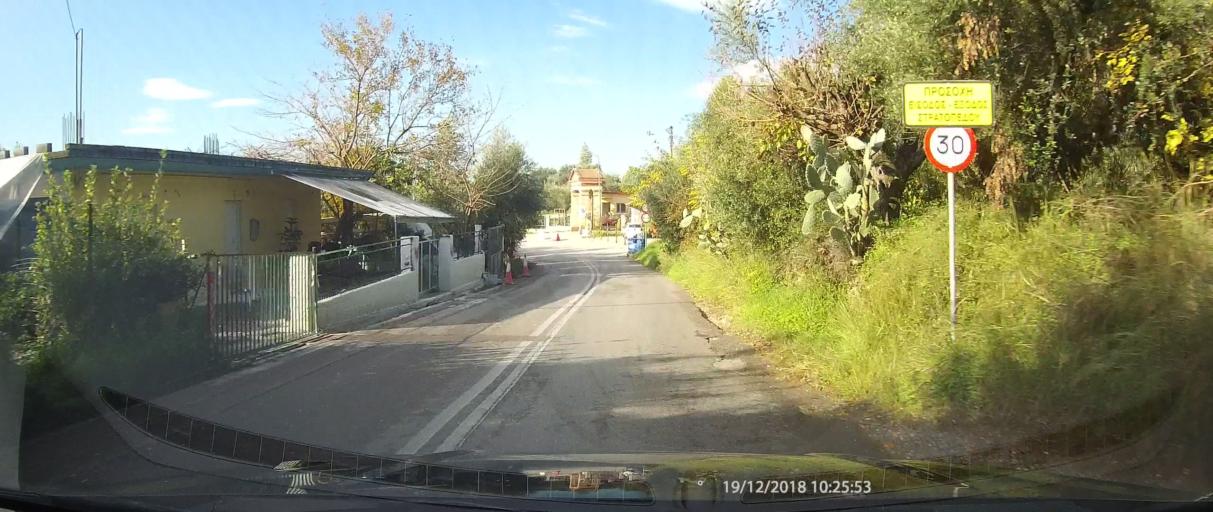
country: GR
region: Peloponnese
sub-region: Nomos Messinias
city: Kalamata
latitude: 37.0465
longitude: 22.1279
